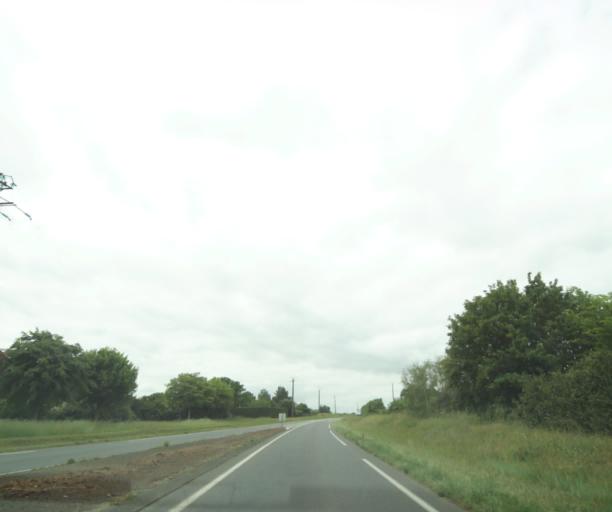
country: FR
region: Pays de la Loire
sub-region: Departement de Maine-et-Loire
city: Montreuil-Bellay
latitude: 47.1426
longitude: -0.1540
